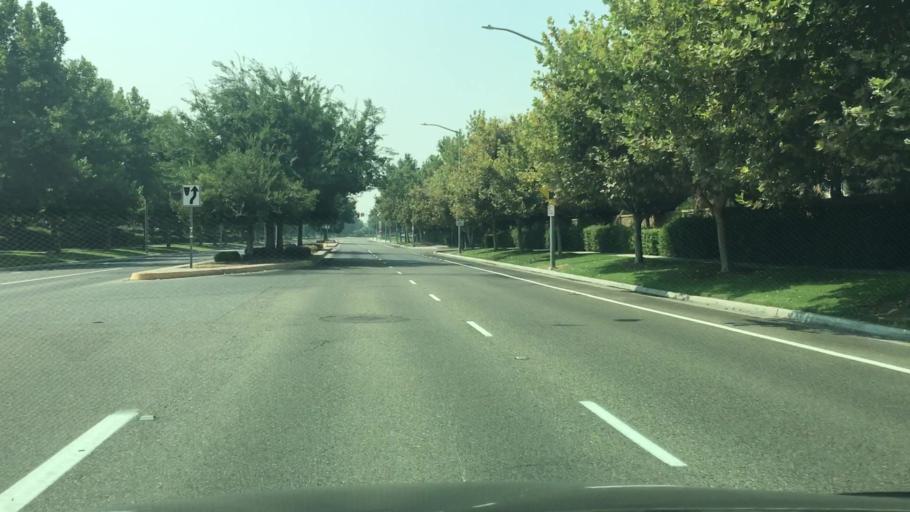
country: US
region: California
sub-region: Fresno County
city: Clovis
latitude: 36.8631
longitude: -119.7022
